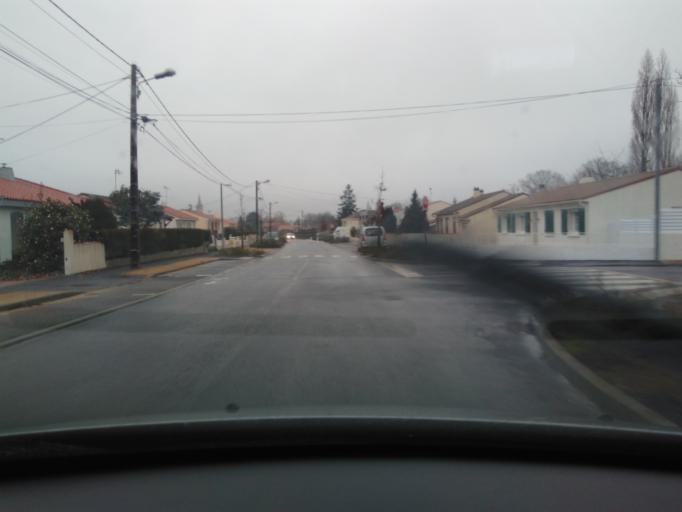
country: FR
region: Pays de la Loire
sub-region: Departement de la Vendee
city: La Ferriere
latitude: 46.7075
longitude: -1.3102
